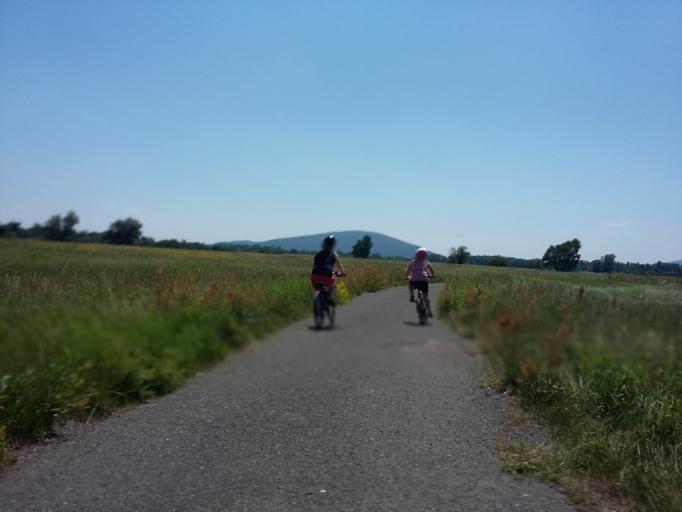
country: AT
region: Lower Austria
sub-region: Politischer Bezirk Ganserndorf
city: Marchegg
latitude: 48.2548
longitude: 16.9533
